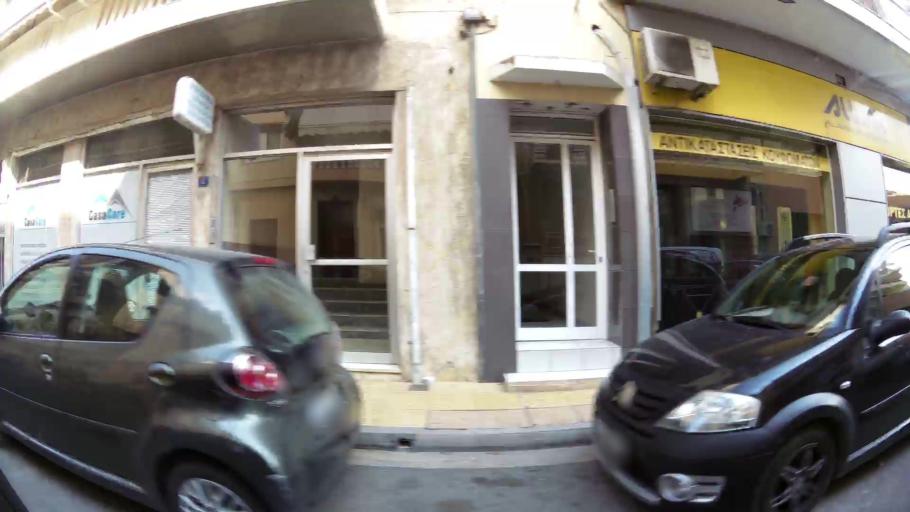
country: GR
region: Attica
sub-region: Nomarchia Athinas
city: Athens
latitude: 38.0011
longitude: 23.7145
